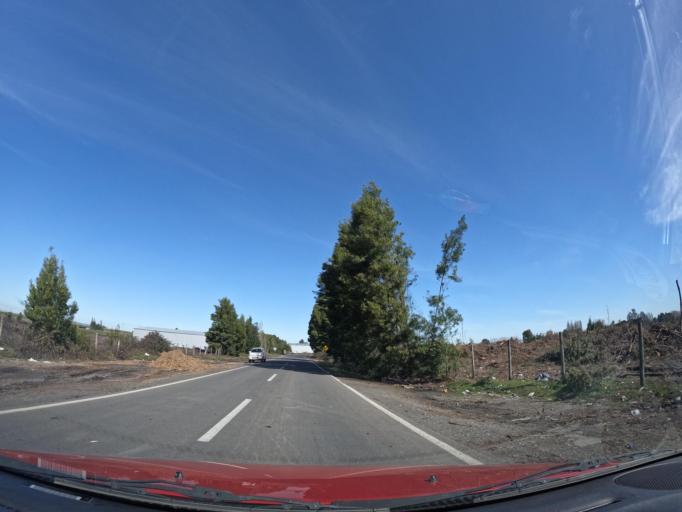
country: CL
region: Biobio
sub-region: Provincia de Biobio
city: Cabrero
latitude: -37.0380
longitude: -72.3732
